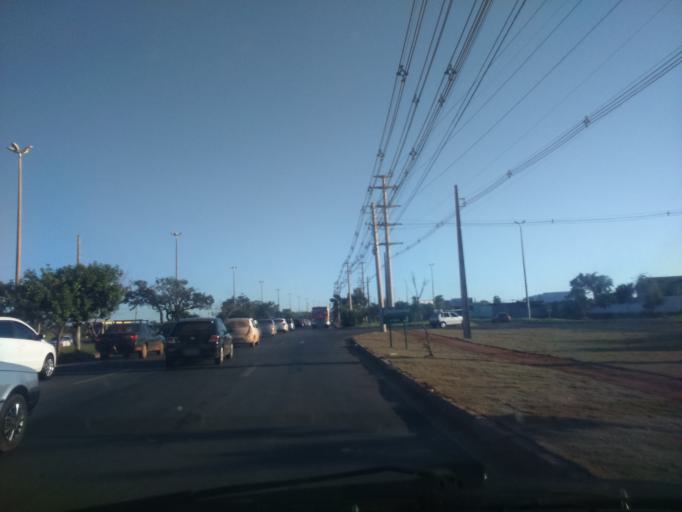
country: BR
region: Federal District
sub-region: Brasilia
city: Brasilia
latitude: -15.8821
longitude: -47.8226
